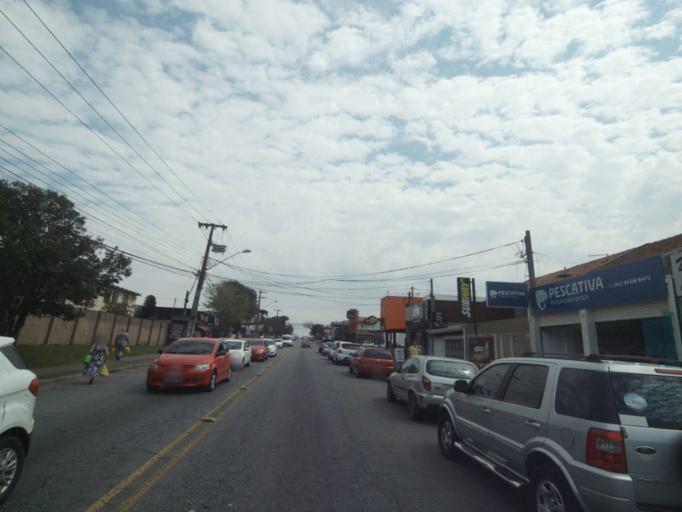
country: BR
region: Parana
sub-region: Pinhais
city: Pinhais
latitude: -25.3997
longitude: -49.2072
